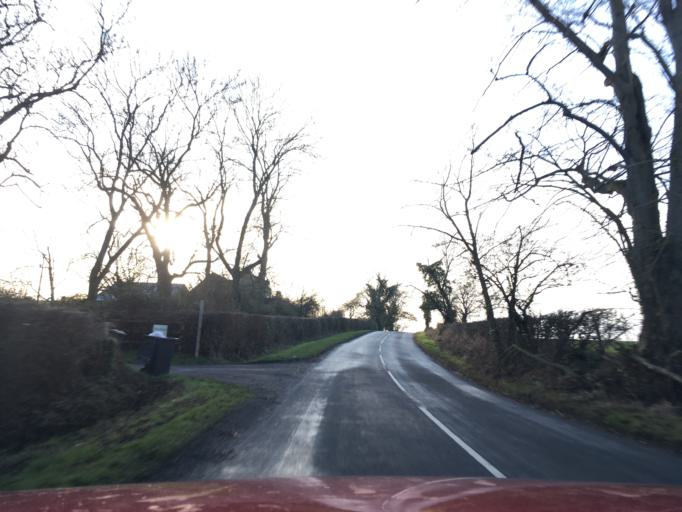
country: GB
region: England
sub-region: Warwickshire
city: Henley in Arden
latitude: 52.2451
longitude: -1.7806
